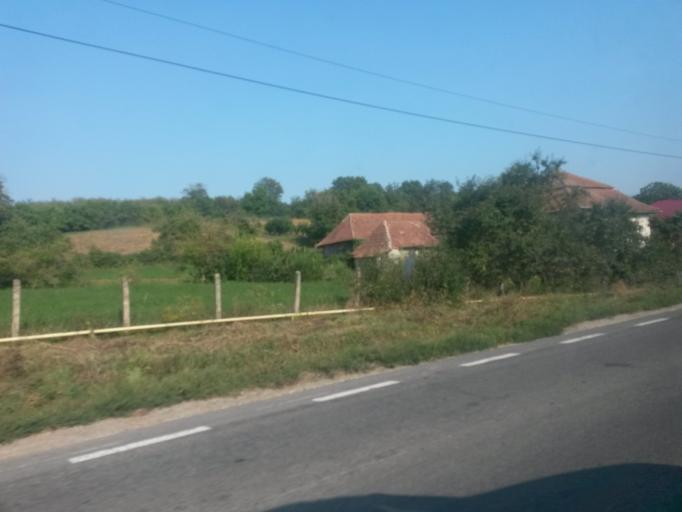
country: RO
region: Alba
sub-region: Comuna Unirea
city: Unirea
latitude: 46.4105
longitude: 23.8085
